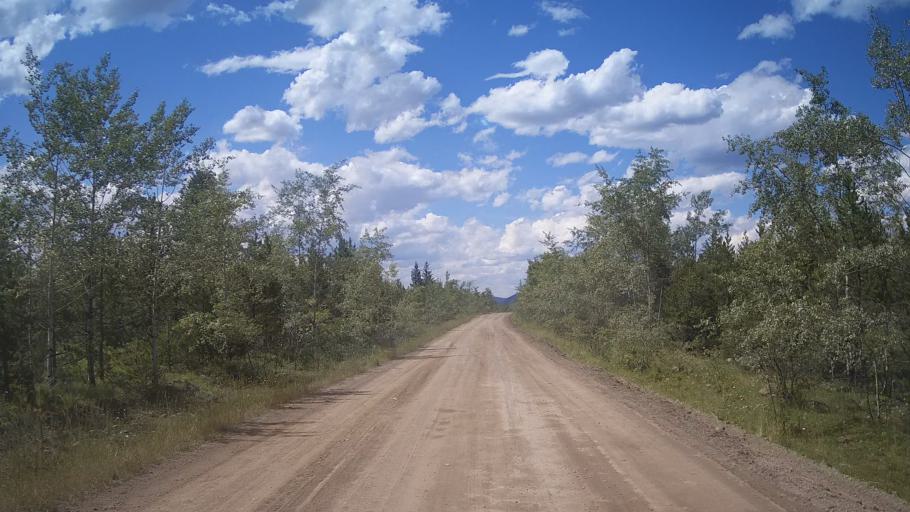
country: CA
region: British Columbia
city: Lillooet
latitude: 51.3398
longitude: -121.9188
